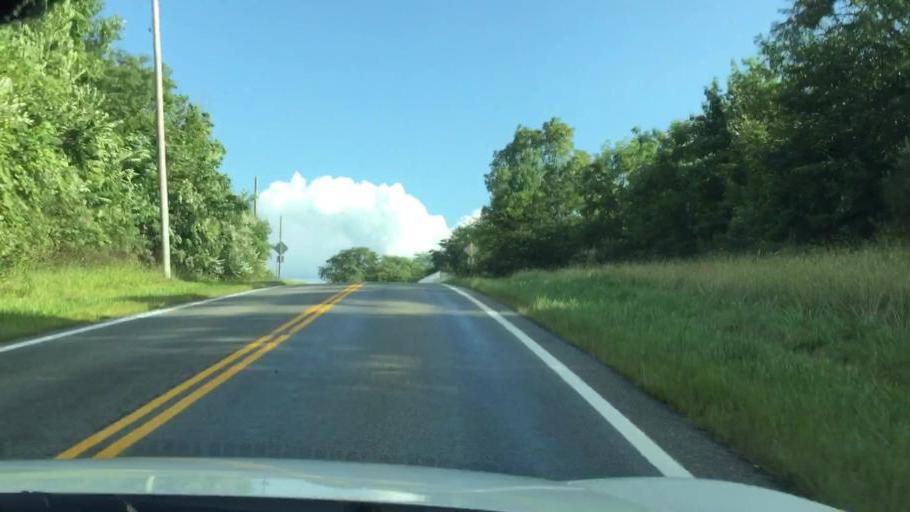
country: US
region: Ohio
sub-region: Champaign County
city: Mechanicsburg
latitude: 40.0395
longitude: -83.6048
